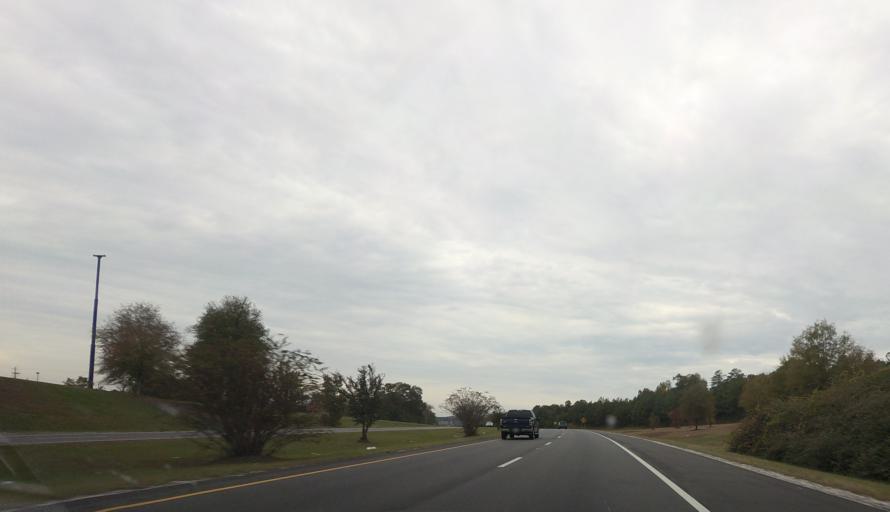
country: US
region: Alabama
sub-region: Russell County
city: Phenix City
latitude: 32.4992
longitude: -85.0180
